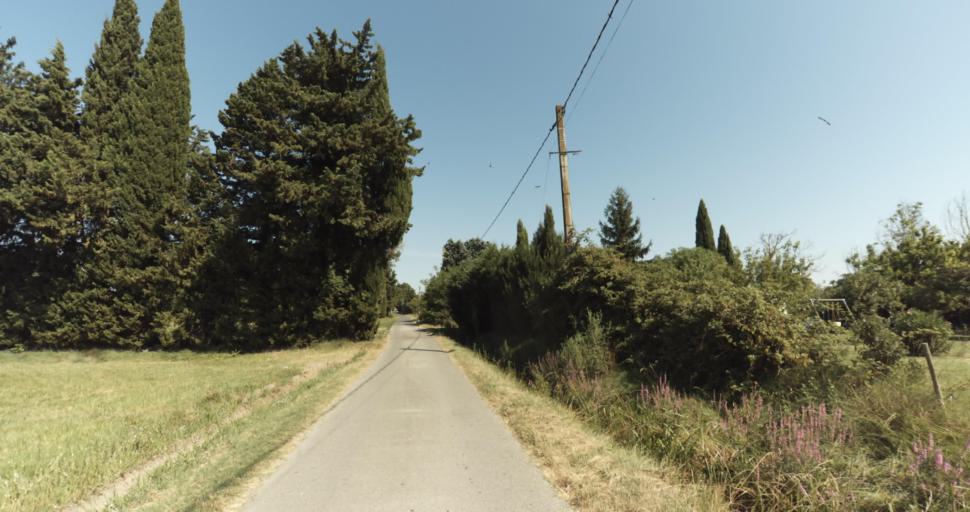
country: FR
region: Provence-Alpes-Cote d'Azur
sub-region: Departement du Vaucluse
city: Monteux
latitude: 44.0132
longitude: 5.0025
